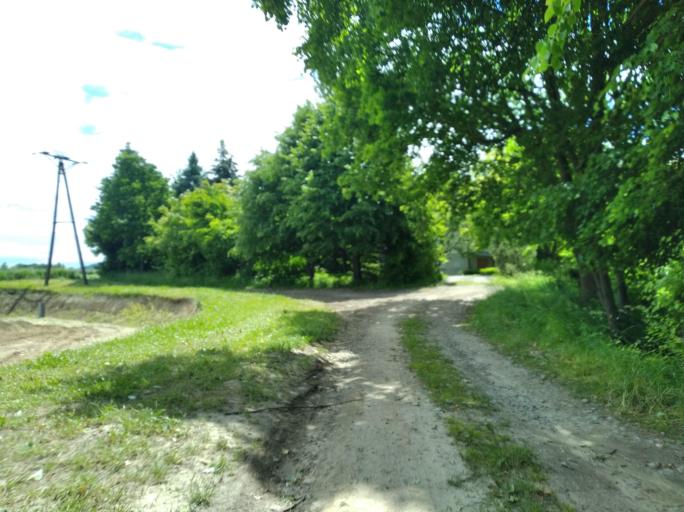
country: PL
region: Subcarpathian Voivodeship
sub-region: Powiat strzyzowski
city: Strzyzow
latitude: 49.8446
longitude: 21.8050
